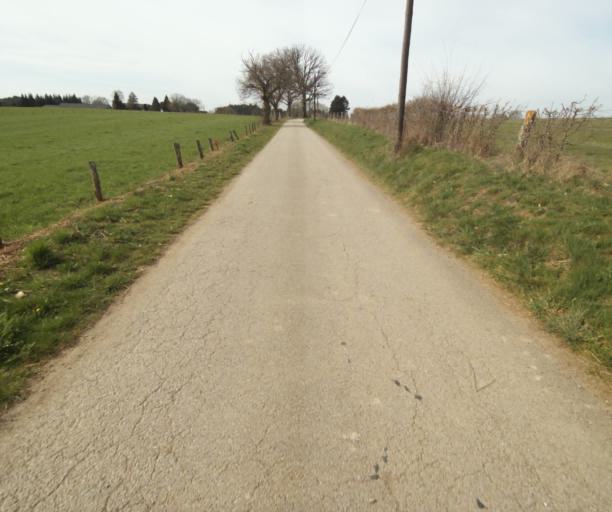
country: FR
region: Limousin
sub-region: Departement de la Correze
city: Correze
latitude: 45.4185
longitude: 1.8214
